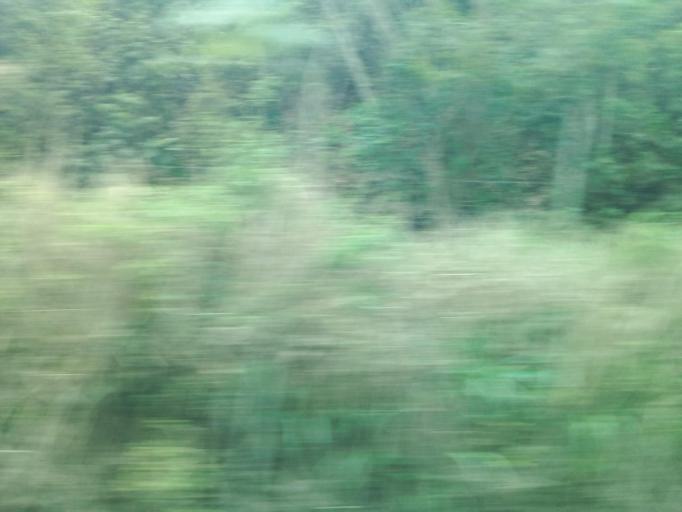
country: BR
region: Minas Gerais
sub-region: Ipaba
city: Ipaba
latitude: -19.4615
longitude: -42.4657
